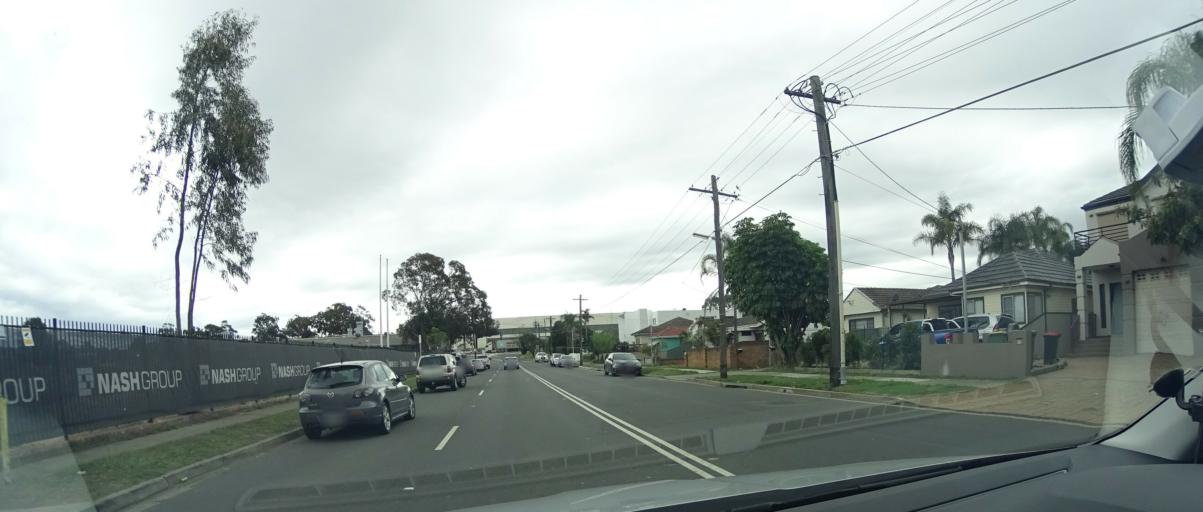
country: AU
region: New South Wales
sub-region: Bankstown
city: Revesby
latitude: -33.9380
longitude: 151.0114
